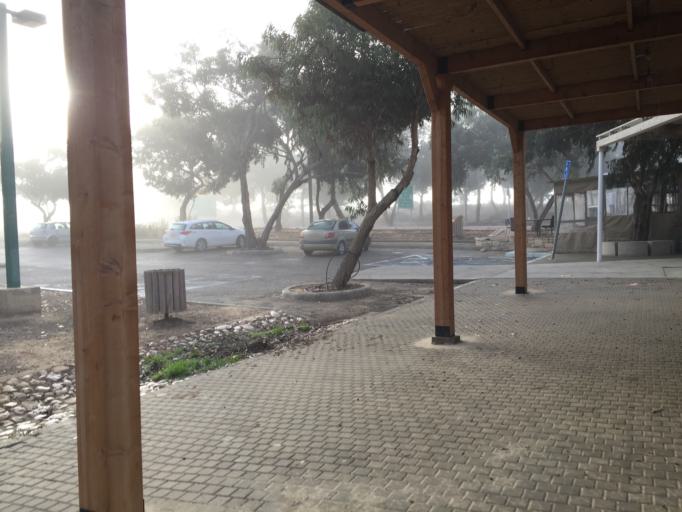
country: IL
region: Southern District
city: Yeroham
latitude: 30.9906
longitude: 34.9101
